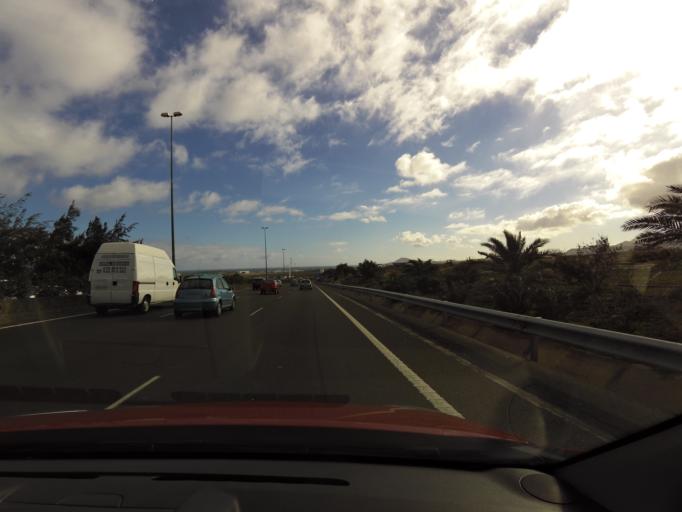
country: ES
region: Canary Islands
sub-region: Provincia de Las Palmas
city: Telde
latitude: 27.9584
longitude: -15.3885
